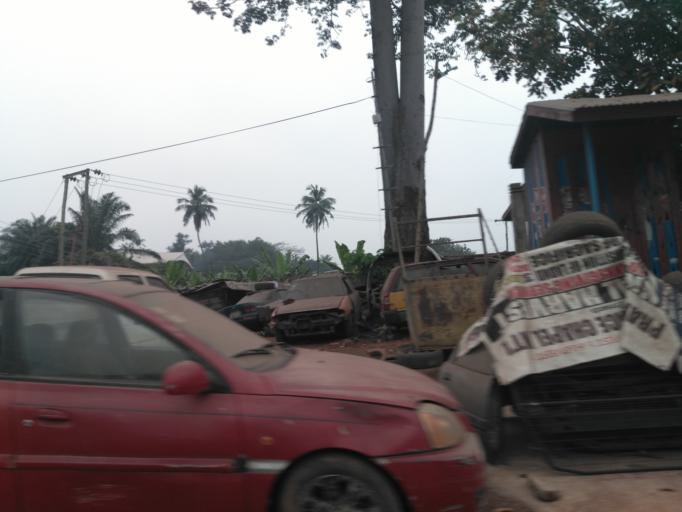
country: GH
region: Ashanti
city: Tafo
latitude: 6.7123
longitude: -1.6215
